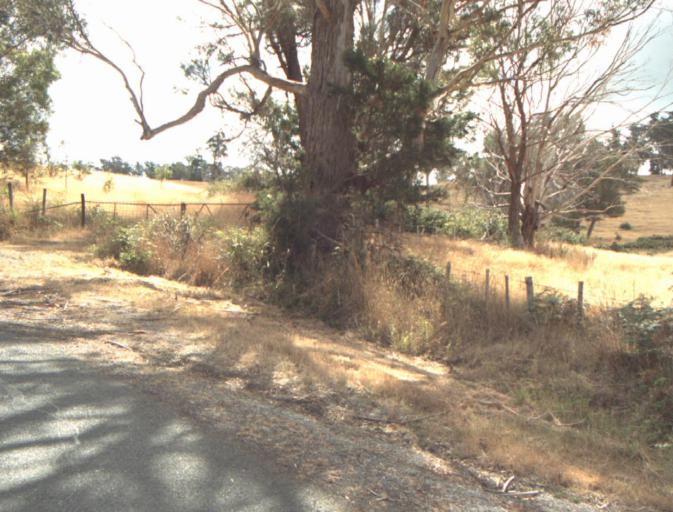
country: AU
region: Tasmania
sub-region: Launceston
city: Mayfield
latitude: -41.3106
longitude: 147.0458
